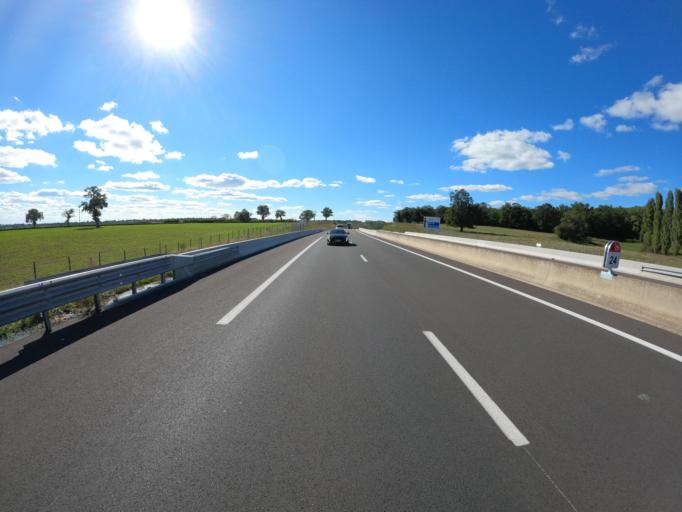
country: FR
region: Auvergne
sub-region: Departement de l'Allier
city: Souvigny
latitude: 46.4391
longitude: 3.1930
